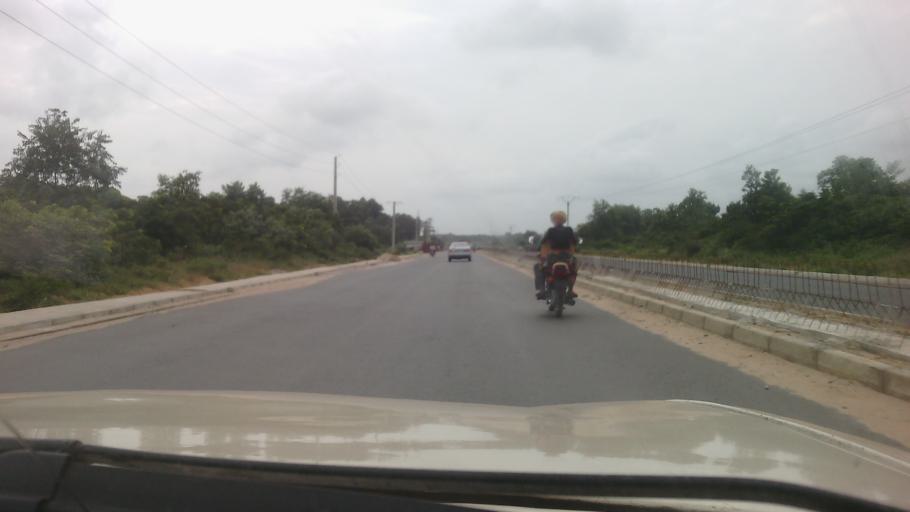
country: BJ
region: Atlantique
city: Ouidah
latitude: 6.3783
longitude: 2.1602
